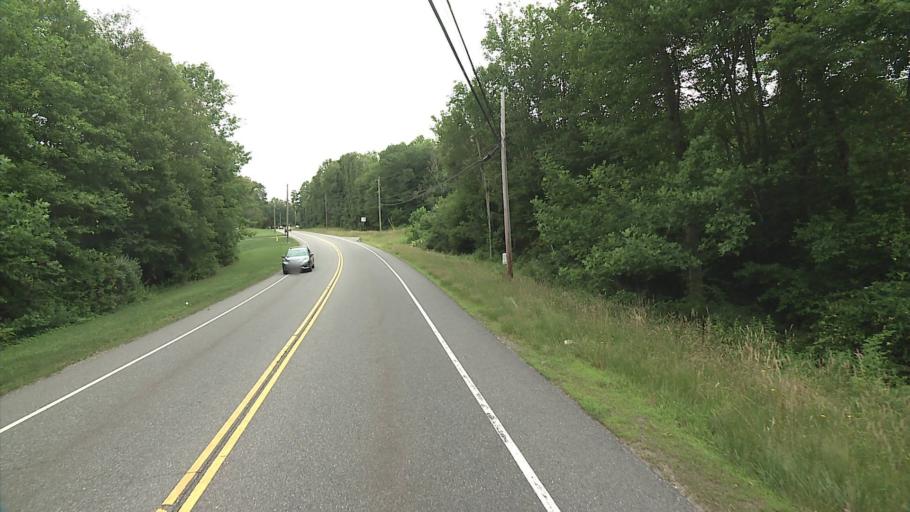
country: US
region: Connecticut
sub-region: New London County
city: Ledyard Center
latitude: 41.4200
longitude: -72.0173
